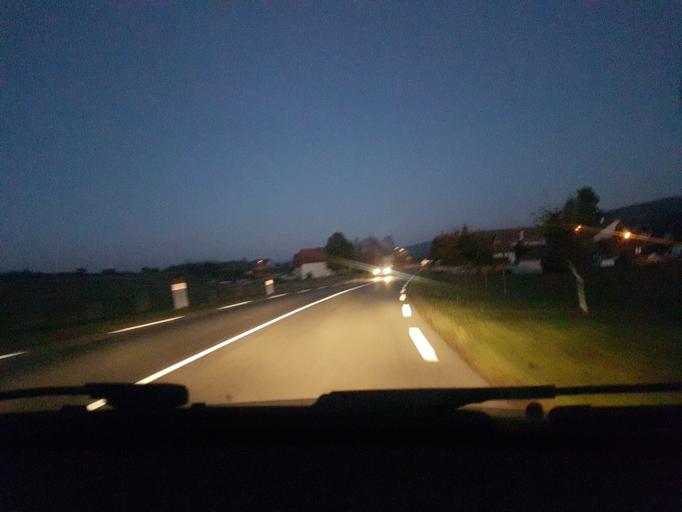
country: FR
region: Franche-Comte
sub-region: Departement du Doubs
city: Villers-le-Lac
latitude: 47.1098
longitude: 6.6815
